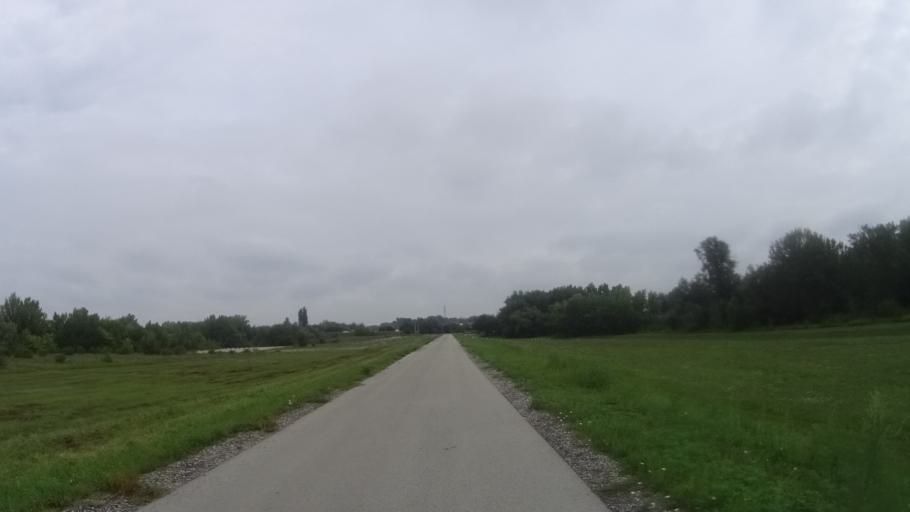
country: SK
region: Nitriansky
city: Komarno
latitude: 47.7583
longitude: 18.1460
